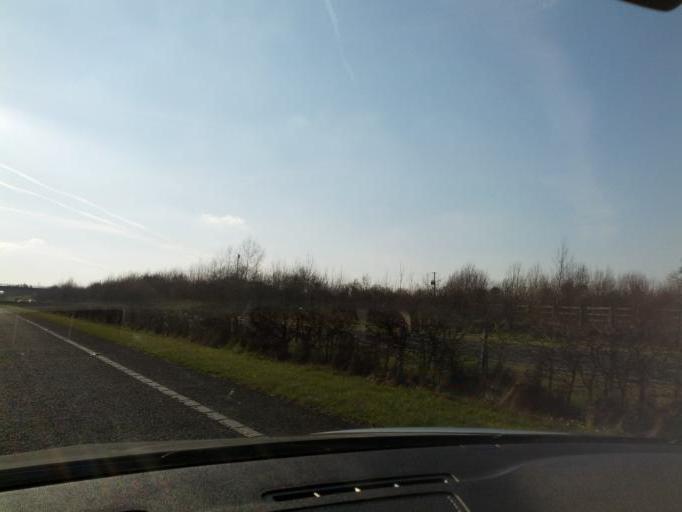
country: IE
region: Leinster
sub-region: Kildare
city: Monasterevin
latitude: 53.1135
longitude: -7.0972
